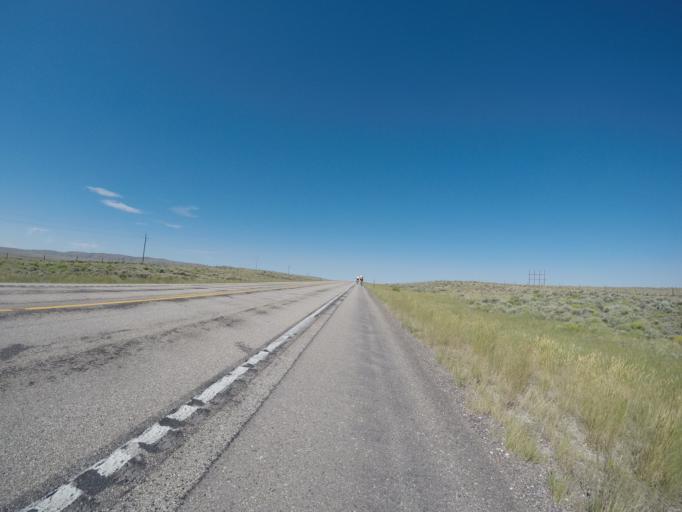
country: US
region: Wyoming
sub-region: Carbon County
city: Saratoga
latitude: 41.8184
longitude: -106.6611
